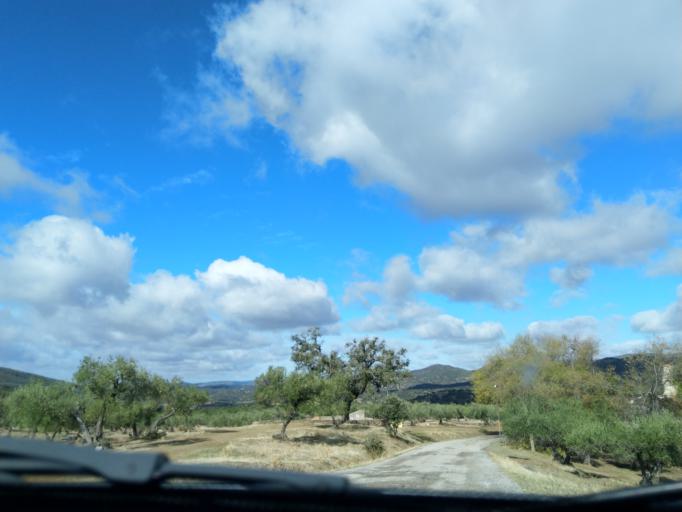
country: ES
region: Extremadura
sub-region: Provincia de Badajoz
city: Reina
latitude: 38.1304
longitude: -5.9395
